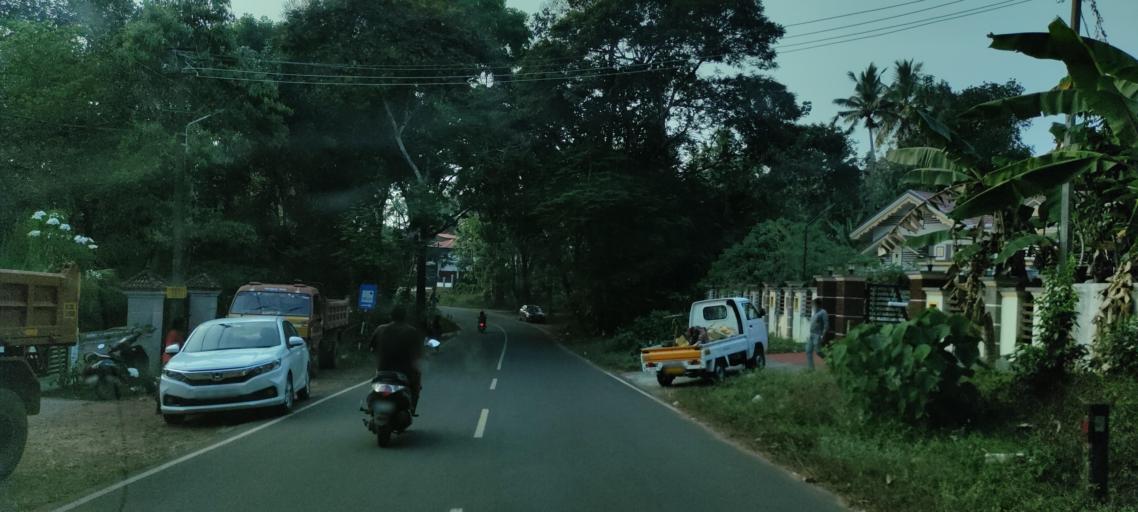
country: IN
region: Kerala
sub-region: Alappuzha
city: Mavelikara
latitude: 9.2502
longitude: 76.5718
